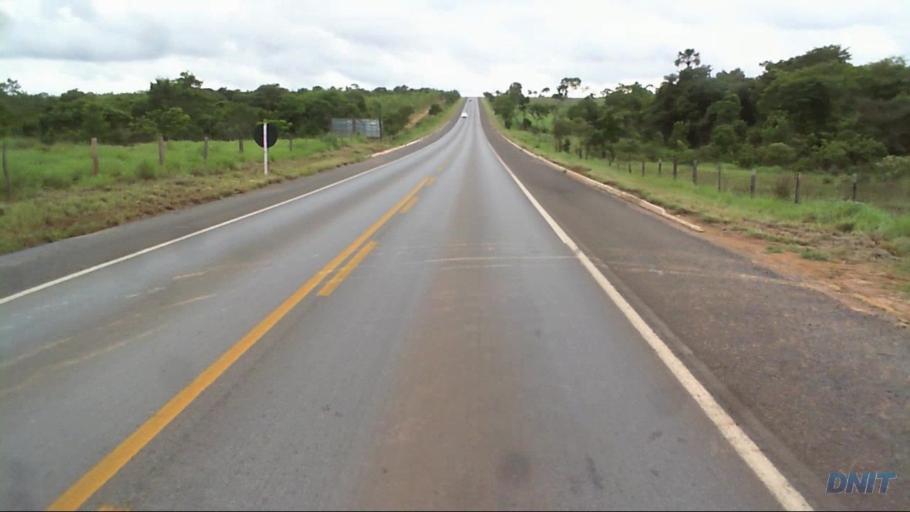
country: BR
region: Goias
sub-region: Barro Alto
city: Barro Alto
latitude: -15.2106
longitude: -48.6683
